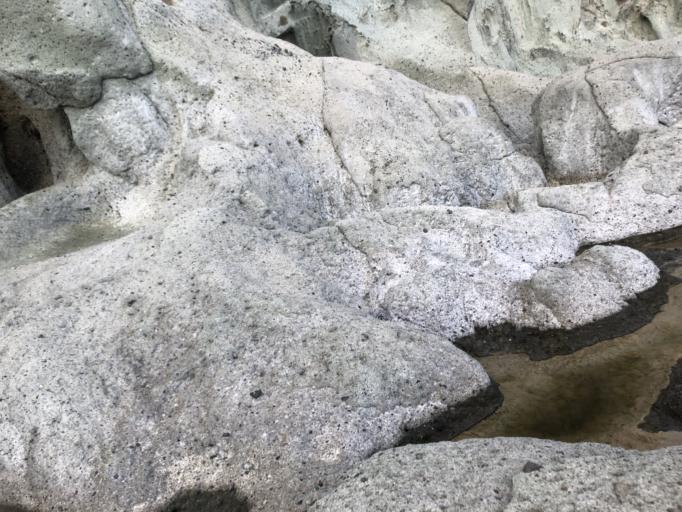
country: IT
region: Sardinia
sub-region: Provincia di Oristano
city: Bosa
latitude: 40.2984
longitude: 8.4680
